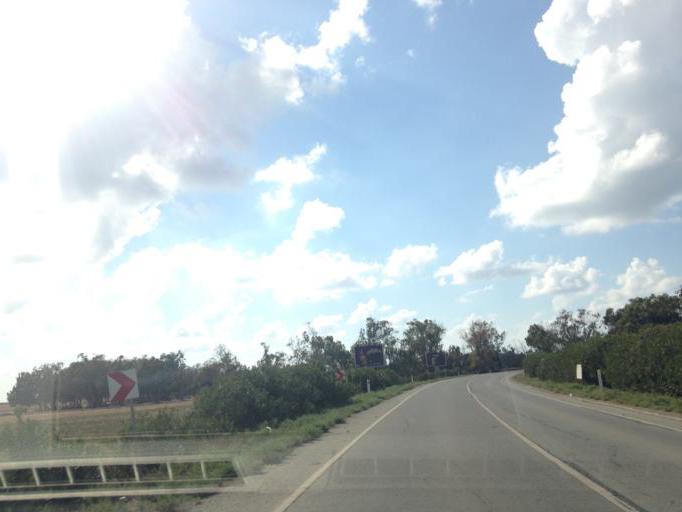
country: CY
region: Pafos
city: Paphos
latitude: 34.7074
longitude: 32.4991
